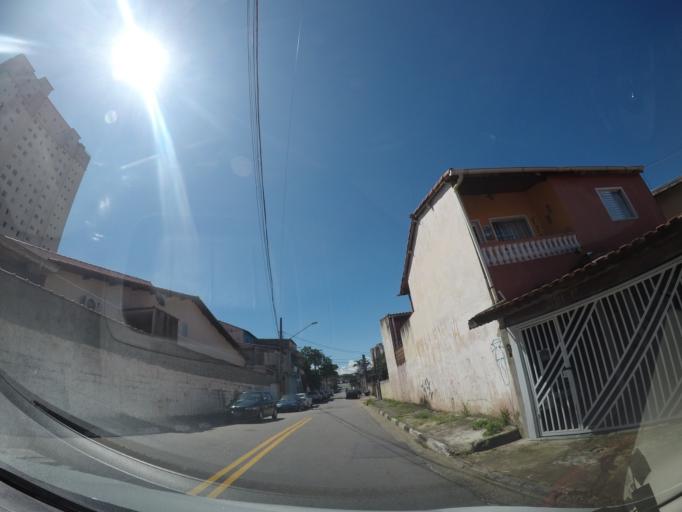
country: BR
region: Sao Paulo
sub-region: Guarulhos
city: Guarulhos
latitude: -23.4571
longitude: -46.5418
